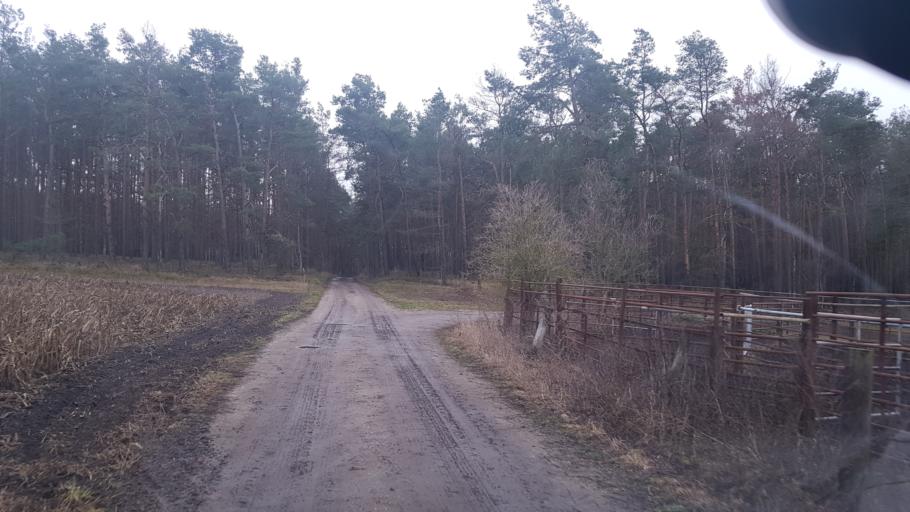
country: DE
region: Brandenburg
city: Ruckersdorf
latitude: 51.6017
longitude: 13.5932
